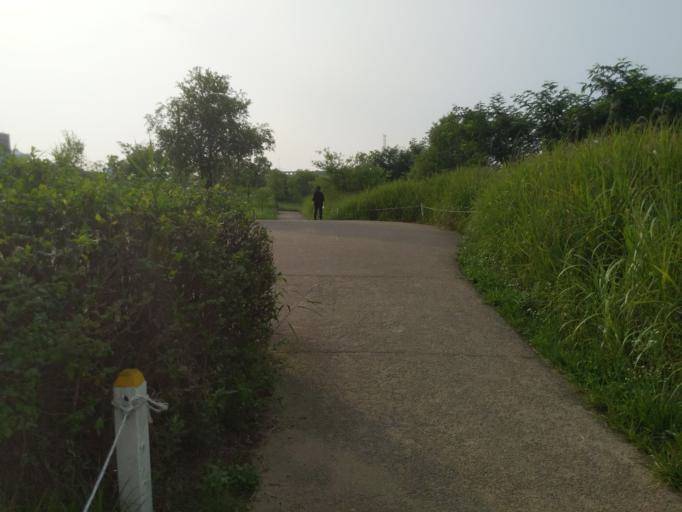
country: KR
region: Gyeonggi-do
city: Kwangmyong
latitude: 37.5380
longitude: 126.9036
